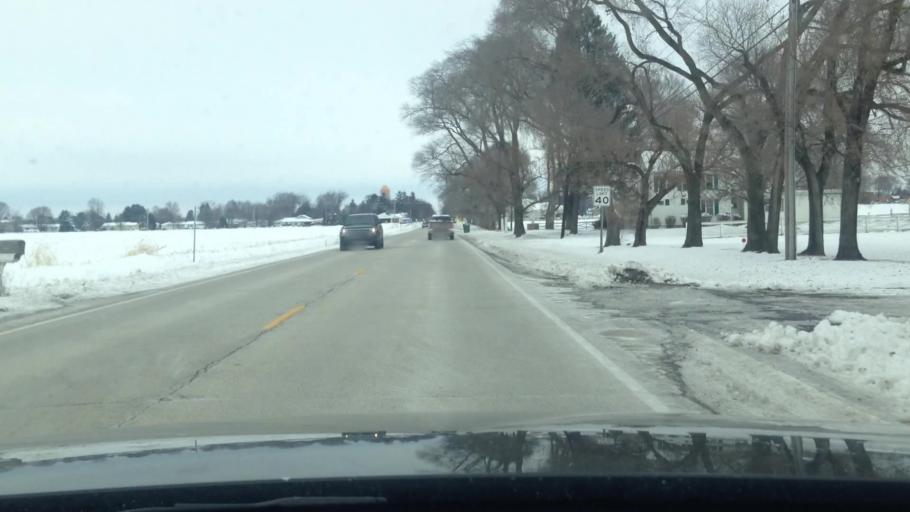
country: US
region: Illinois
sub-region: McHenry County
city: Hebron
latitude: 42.4604
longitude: -88.4328
